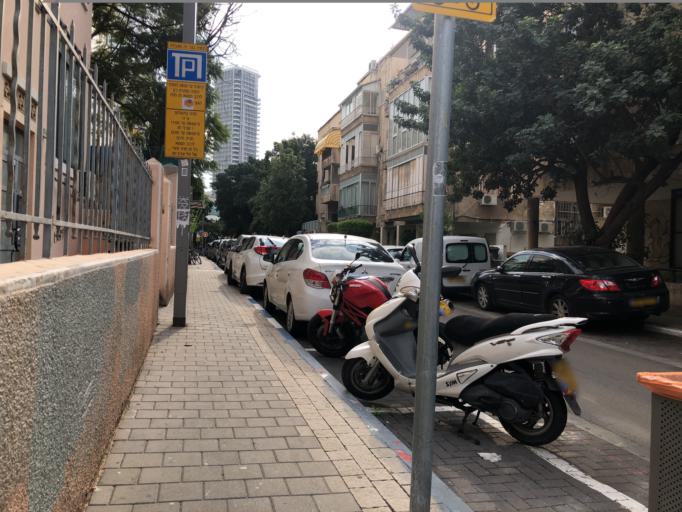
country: IL
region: Tel Aviv
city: Tel Aviv
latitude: 32.0673
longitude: 34.7753
